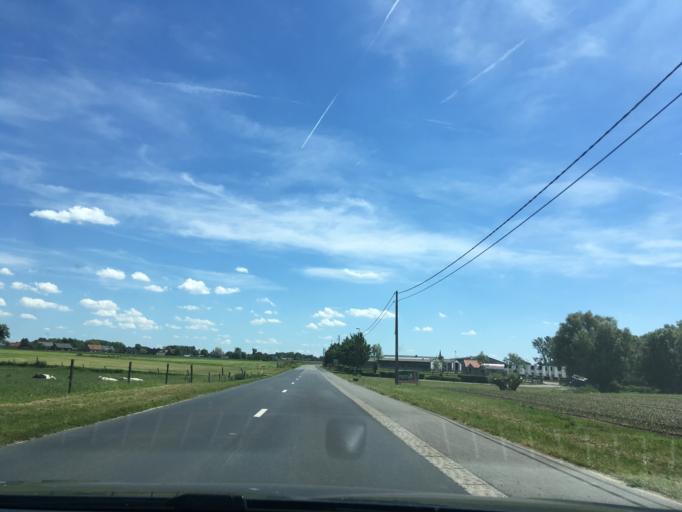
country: BE
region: Flanders
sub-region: Provincie West-Vlaanderen
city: Hooglede
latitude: 51.0079
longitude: 3.0852
